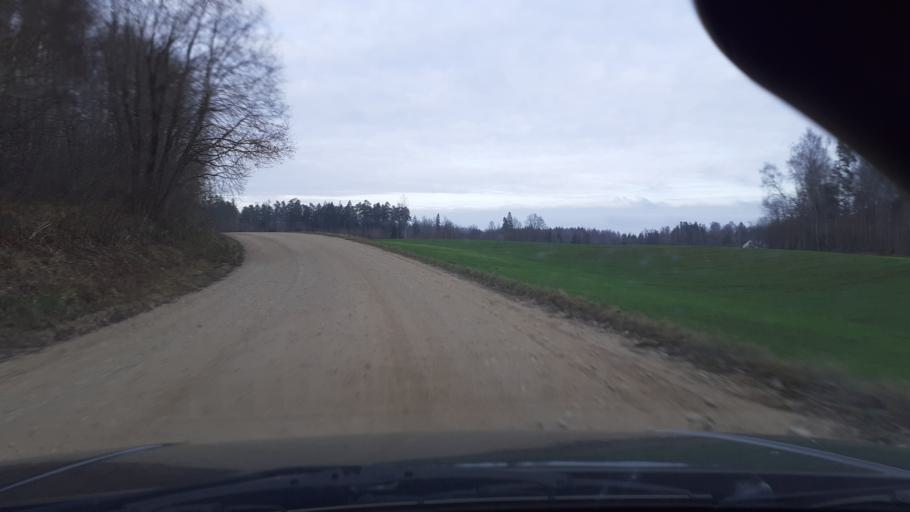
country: LV
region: Alsunga
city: Alsunga
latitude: 56.9594
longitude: 21.6519
